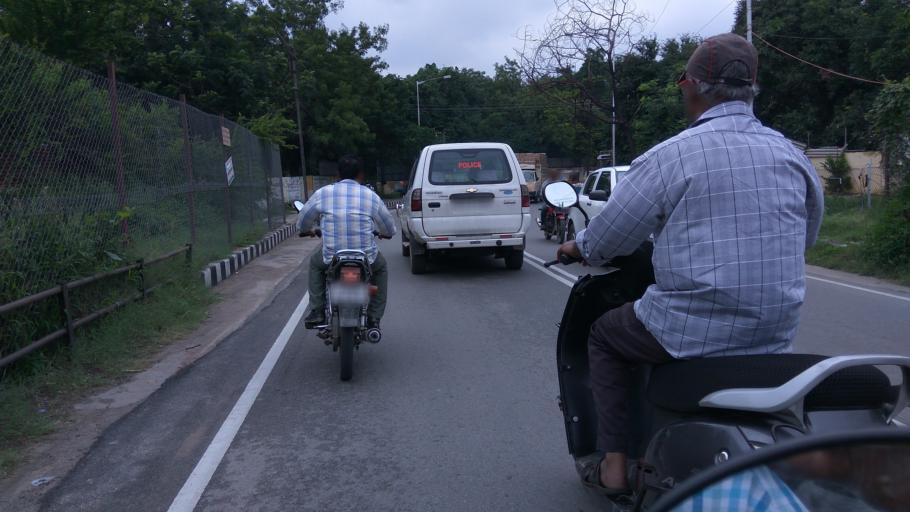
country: IN
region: Telangana
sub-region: Hyderabad
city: Malkajgiri
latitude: 17.4383
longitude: 78.5247
